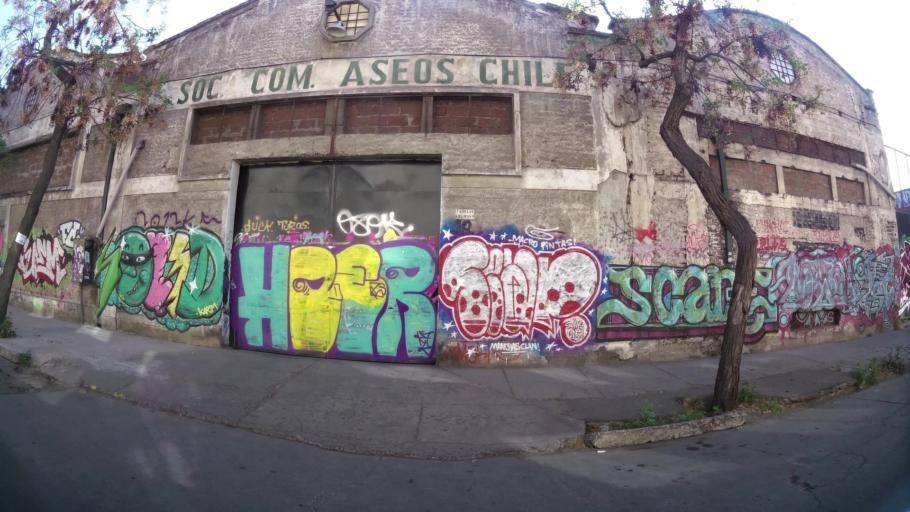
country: CL
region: Santiago Metropolitan
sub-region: Provincia de Santiago
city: Santiago
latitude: -33.4466
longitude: -70.6722
